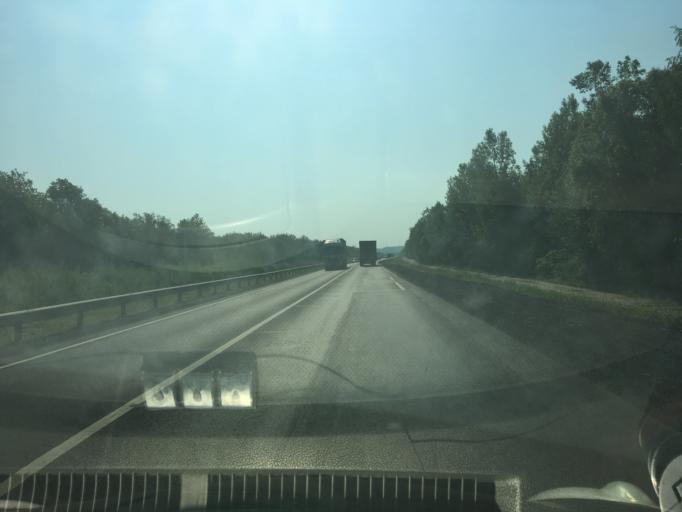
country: RU
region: Nizjnij Novgorod
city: Kstovo
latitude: 56.0922
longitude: 44.3267
